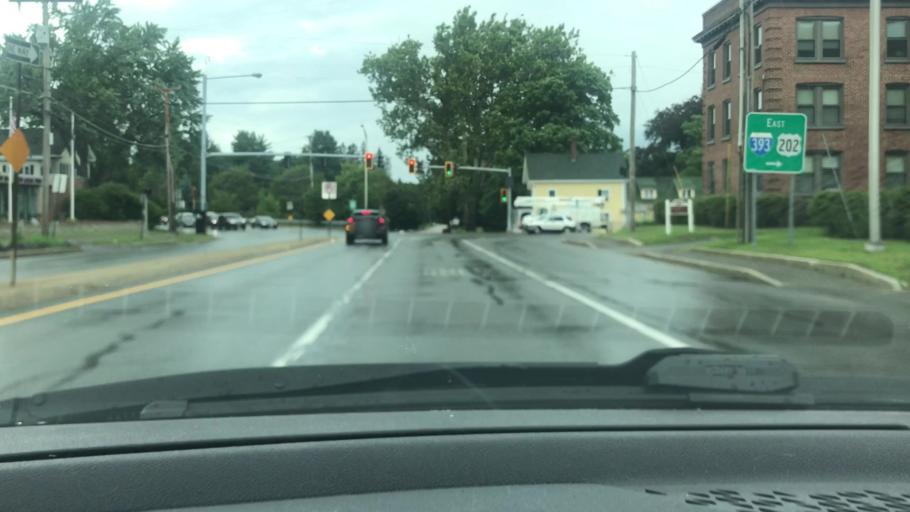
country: US
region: New Hampshire
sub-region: Merrimack County
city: Concord
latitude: 43.2139
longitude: -71.5404
